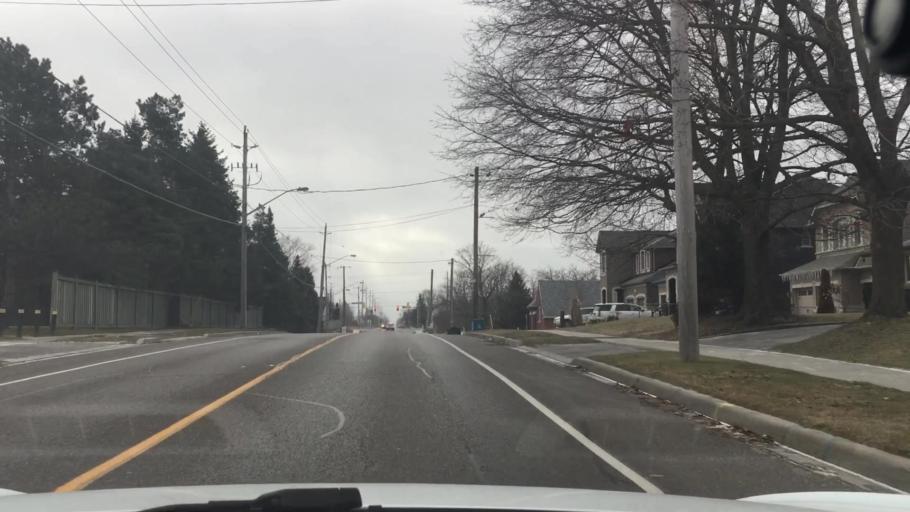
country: CA
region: Ontario
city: Oshawa
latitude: 43.9128
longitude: -78.7893
